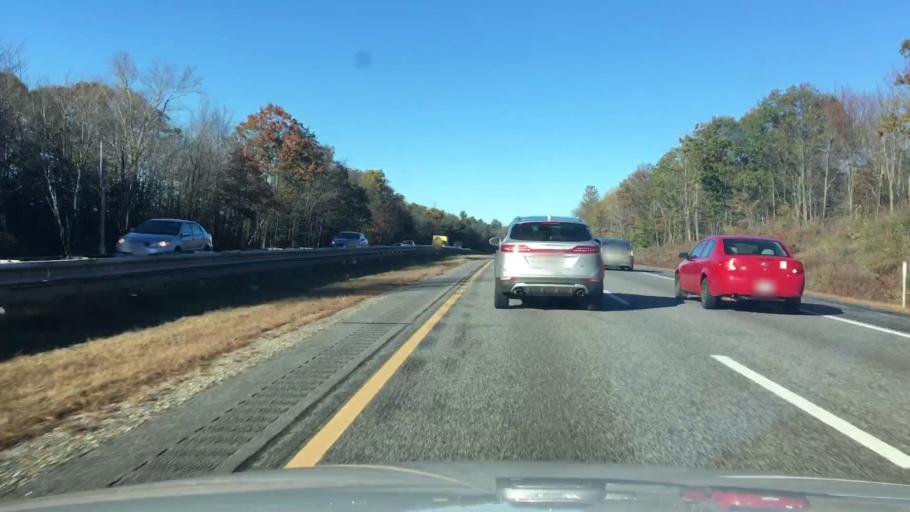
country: US
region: Maine
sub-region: Cumberland County
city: Freeport
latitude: 43.8941
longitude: -70.0784
